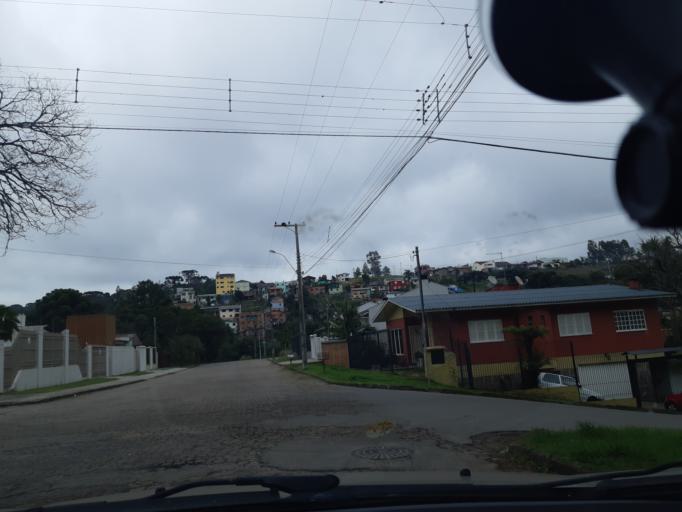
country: BR
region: Rio Grande do Sul
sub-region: Caxias Do Sul
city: Caxias do Sul
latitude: -29.1588
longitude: -51.2053
